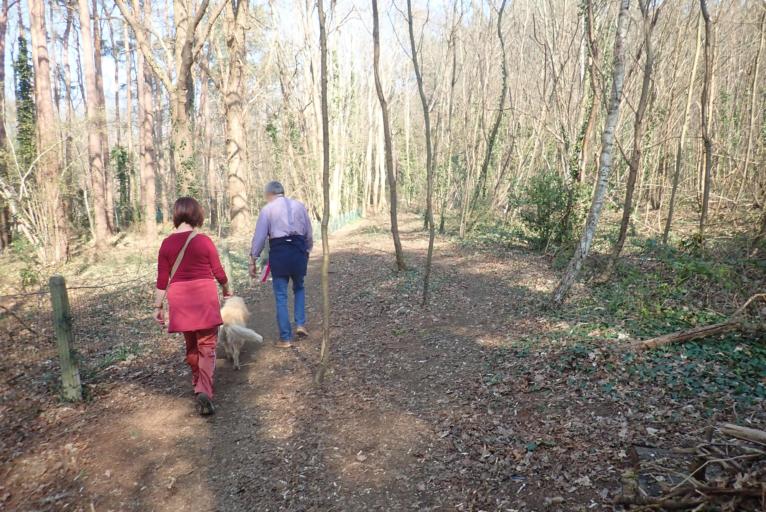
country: BE
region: Flanders
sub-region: Provincie Vlaams-Brabant
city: Aarschot
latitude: 50.9978
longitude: 4.8564
